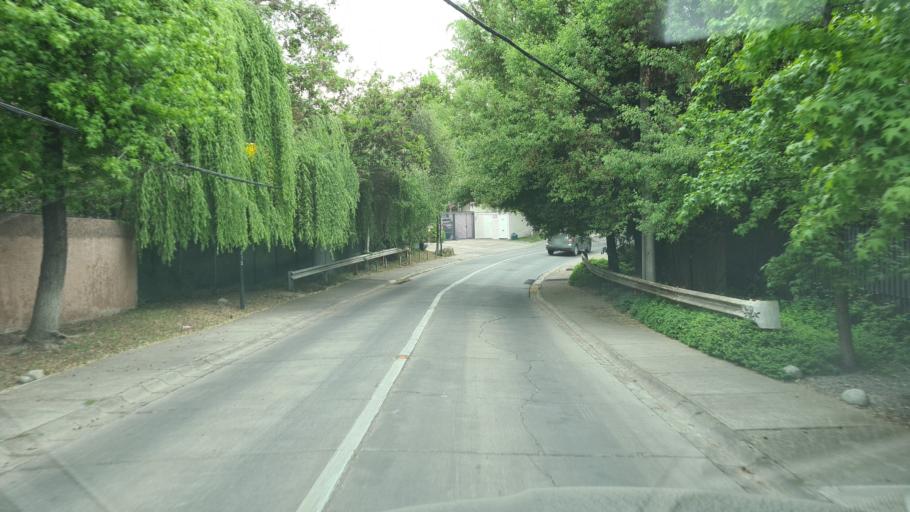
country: CL
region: Santiago Metropolitan
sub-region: Provincia de Santiago
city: Villa Presidente Frei, Nunoa, Santiago, Chile
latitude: -33.3424
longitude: -70.5071
